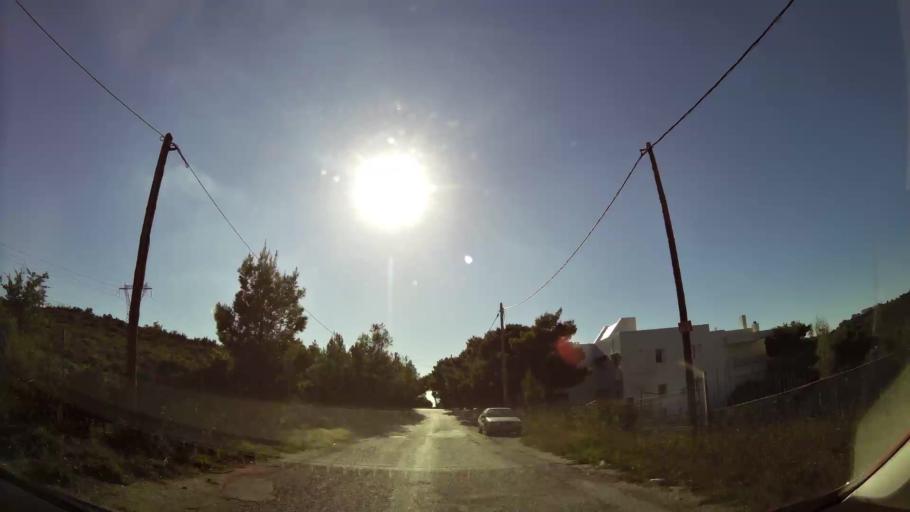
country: GR
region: Attica
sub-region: Nomarchia Anatolikis Attikis
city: Anthousa
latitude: 38.0407
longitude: 23.8817
